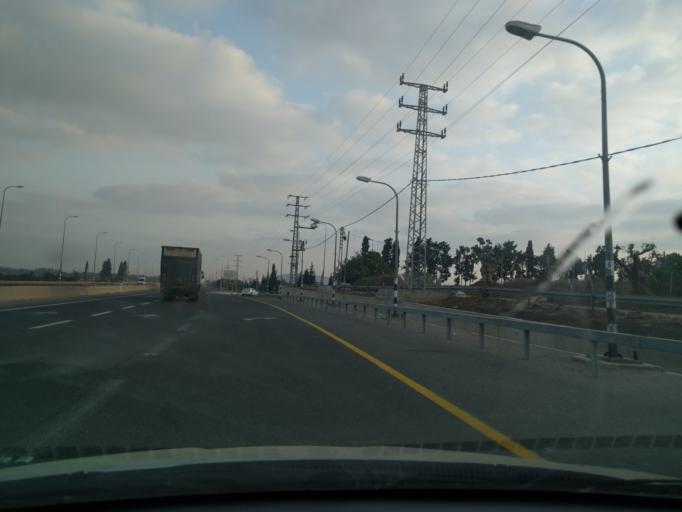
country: IL
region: Haifa
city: Qesarya
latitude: 32.5076
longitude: 34.9308
